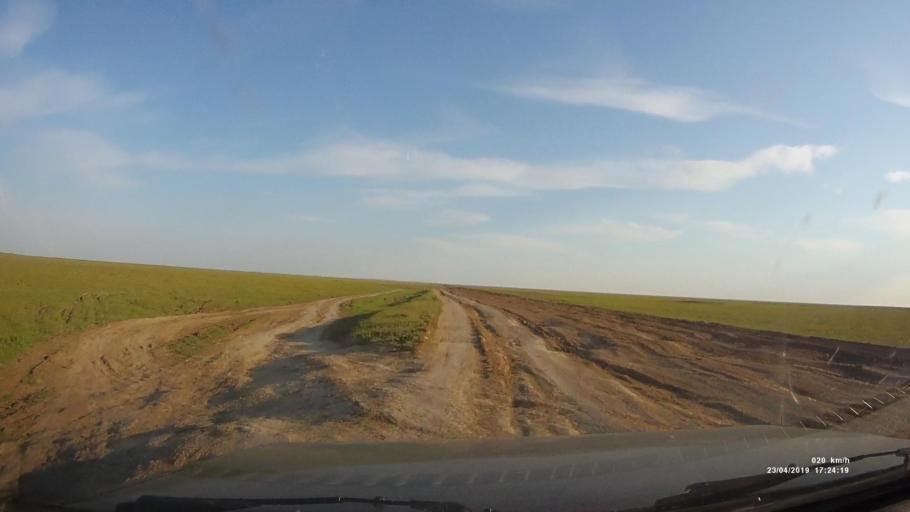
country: RU
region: Kalmykiya
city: Priyutnoye
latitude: 46.1575
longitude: 43.5085
